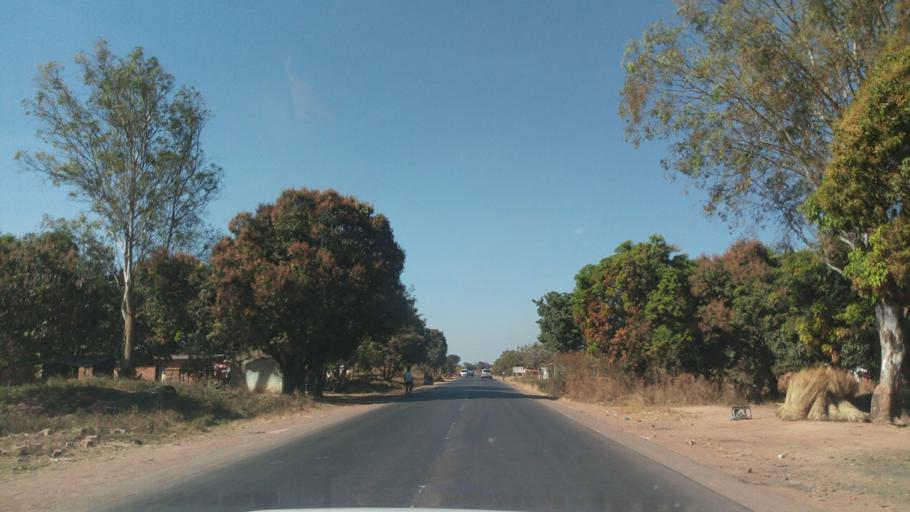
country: CD
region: Katanga
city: Lubumbashi
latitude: -11.5563
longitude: 27.5793
